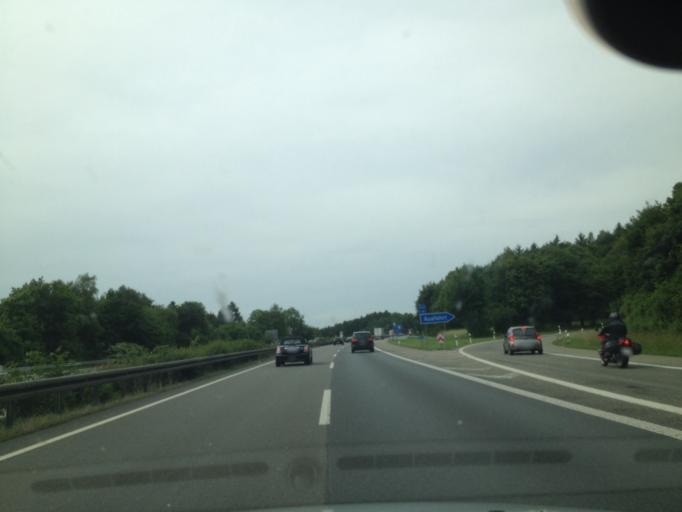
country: DE
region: North Rhine-Westphalia
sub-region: Regierungsbezirk Arnsberg
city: Luedenscheid
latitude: 51.2616
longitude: 7.6041
